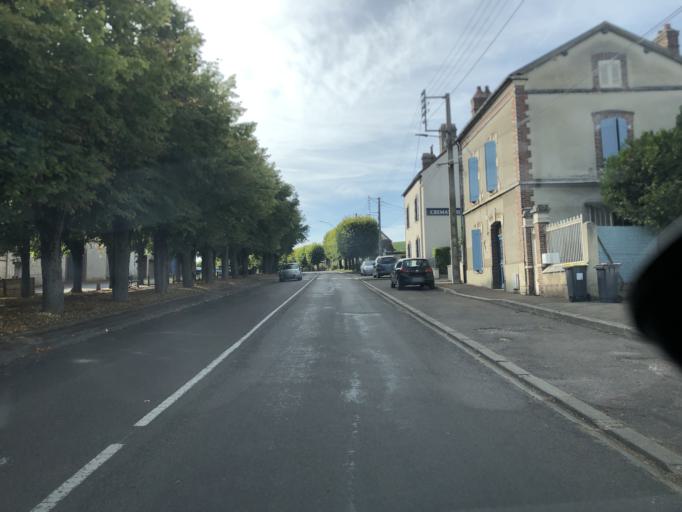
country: FR
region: Bourgogne
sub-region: Departement de l'Yonne
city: Joigny
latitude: 47.9842
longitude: 3.4001
